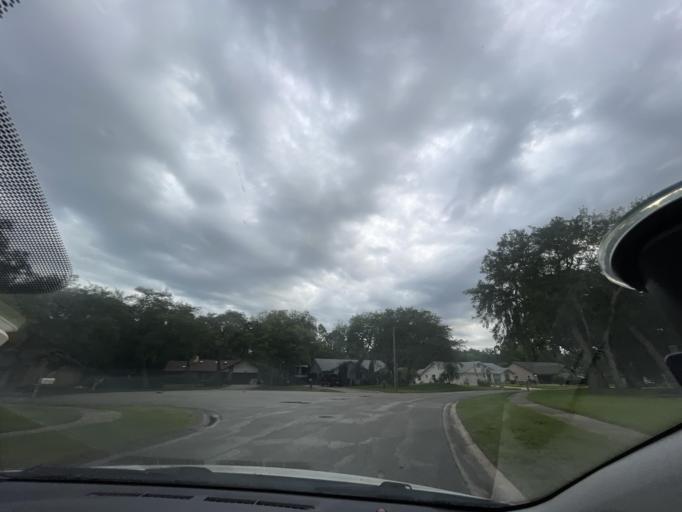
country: US
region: Florida
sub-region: Volusia County
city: Port Orange
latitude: 29.0895
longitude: -80.9982
